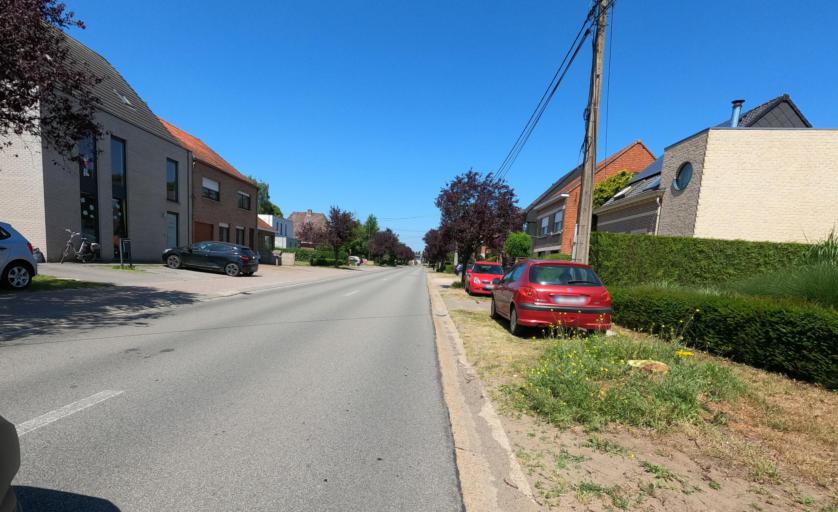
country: BE
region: Flanders
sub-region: Provincie Antwerpen
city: Zandhoven
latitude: 51.2228
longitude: 4.6682
